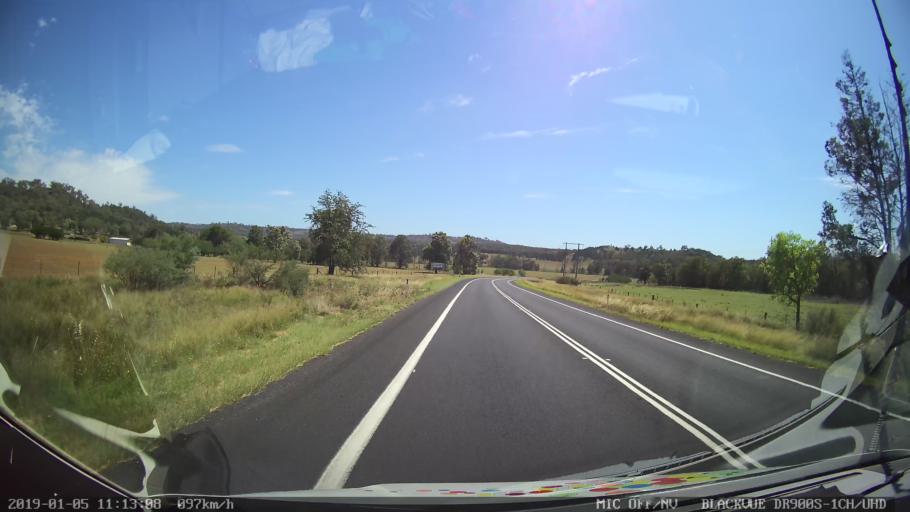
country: AU
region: New South Wales
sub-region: Warrumbungle Shire
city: Coonabarabran
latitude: -31.3739
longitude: 149.2674
